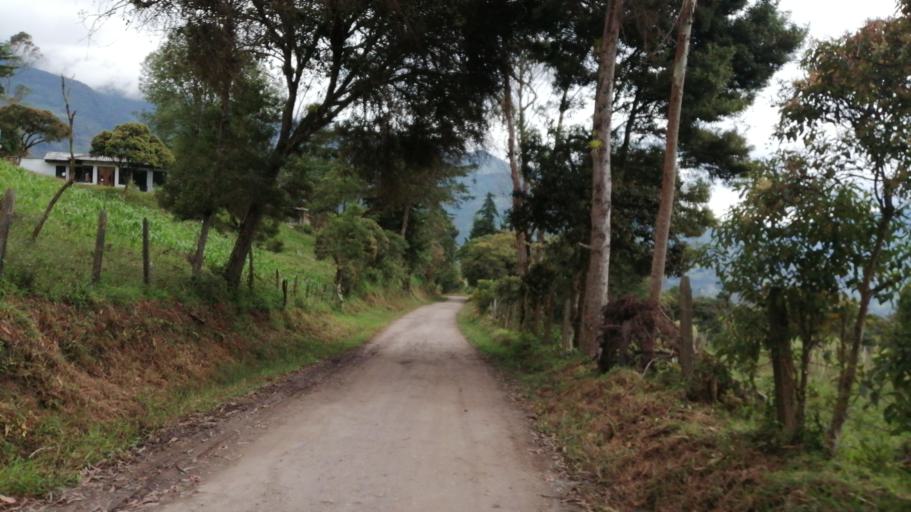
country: CO
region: Boyaca
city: Chinavita
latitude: 5.1308
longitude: -73.3966
